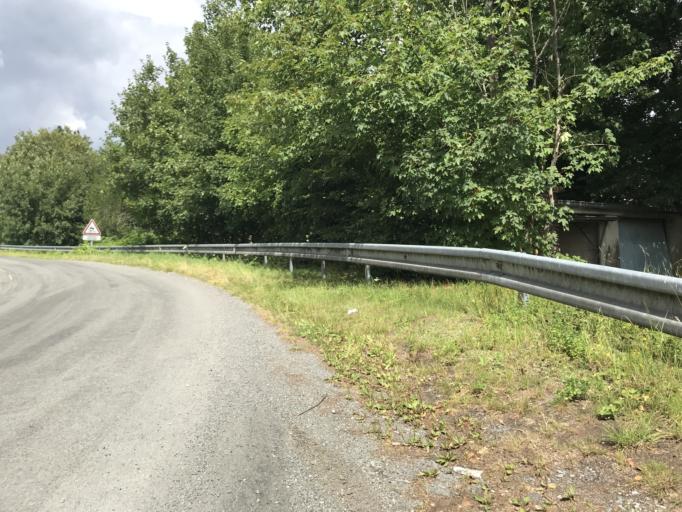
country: FR
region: Champagne-Ardenne
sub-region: Departement des Ardennes
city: Montherme
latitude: 49.8860
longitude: 4.7462
